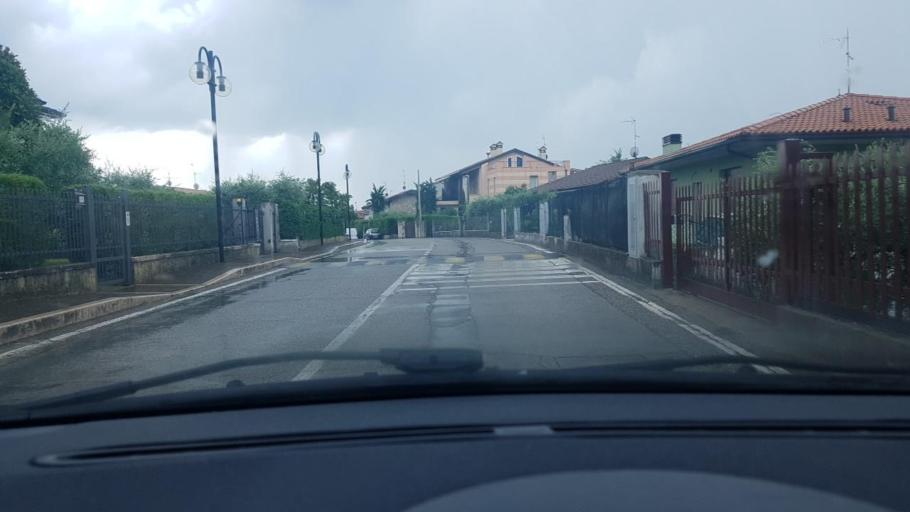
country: IT
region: Veneto
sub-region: Provincia di Verona
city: Costermano
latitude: 45.6051
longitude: 10.7272
